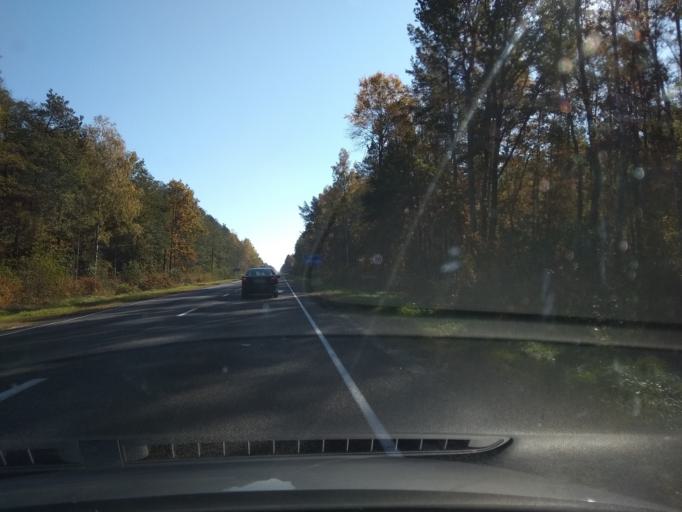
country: BY
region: Brest
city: Malaryta
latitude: 51.8951
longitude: 24.1338
